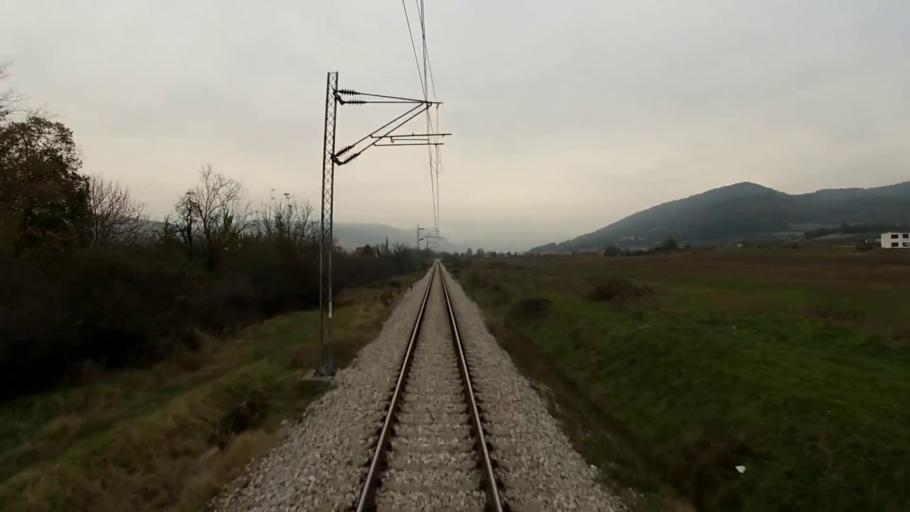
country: RS
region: Central Serbia
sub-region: Pirotski Okrug
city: Dimitrovgrad
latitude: 43.0043
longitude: 22.8123
